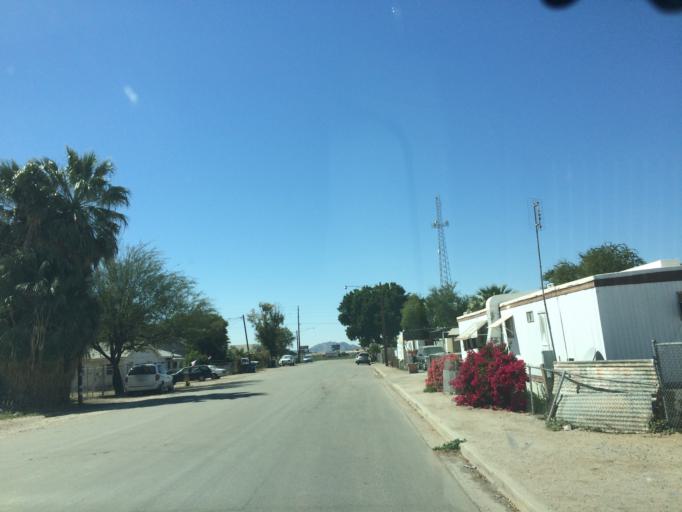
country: US
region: Arizona
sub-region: Yuma County
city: Yuma
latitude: 32.7377
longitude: -114.6358
